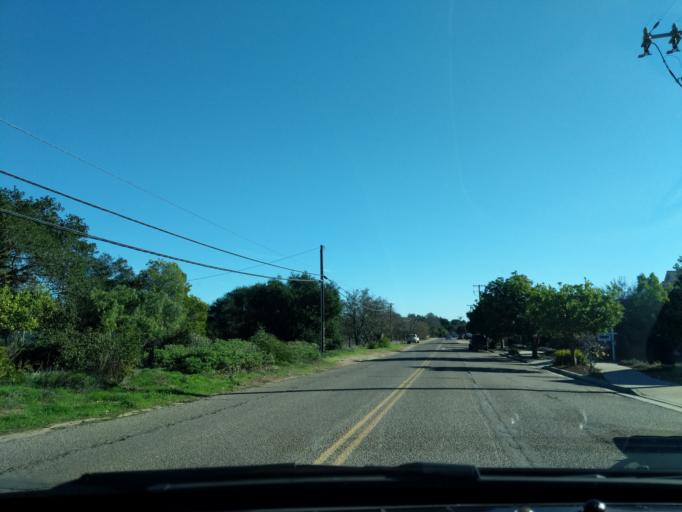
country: US
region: California
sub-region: San Luis Obispo County
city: Nipomo
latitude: 35.0358
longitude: -120.4809
